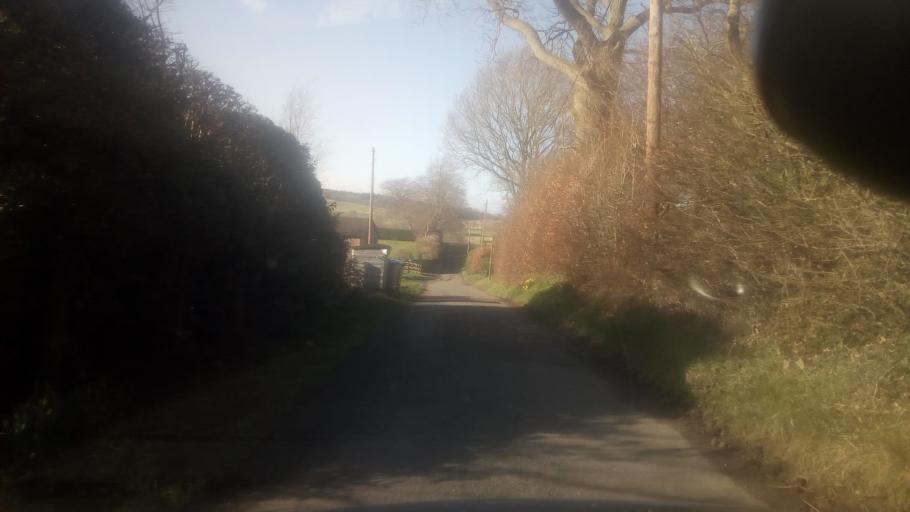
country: GB
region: Scotland
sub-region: The Scottish Borders
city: Jedburgh
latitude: 55.4861
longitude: -2.5360
